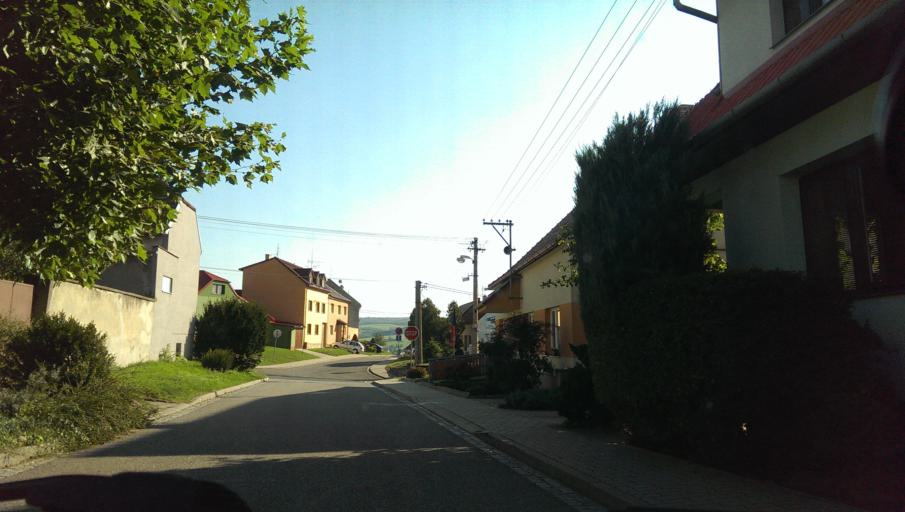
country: CZ
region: Zlin
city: Popovice
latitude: 49.0527
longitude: 17.5243
